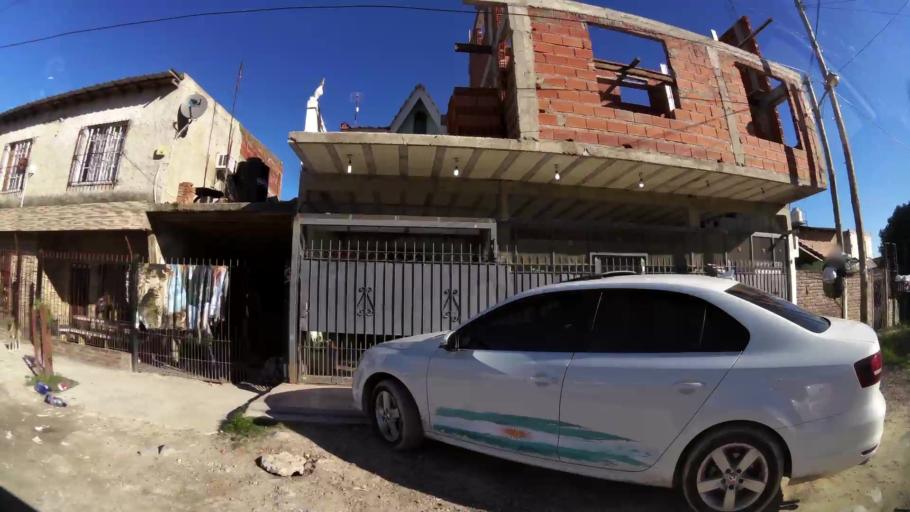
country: AR
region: Buenos Aires
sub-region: Partido de Quilmes
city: Quilmes
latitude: -34.7447
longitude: -58.3196
